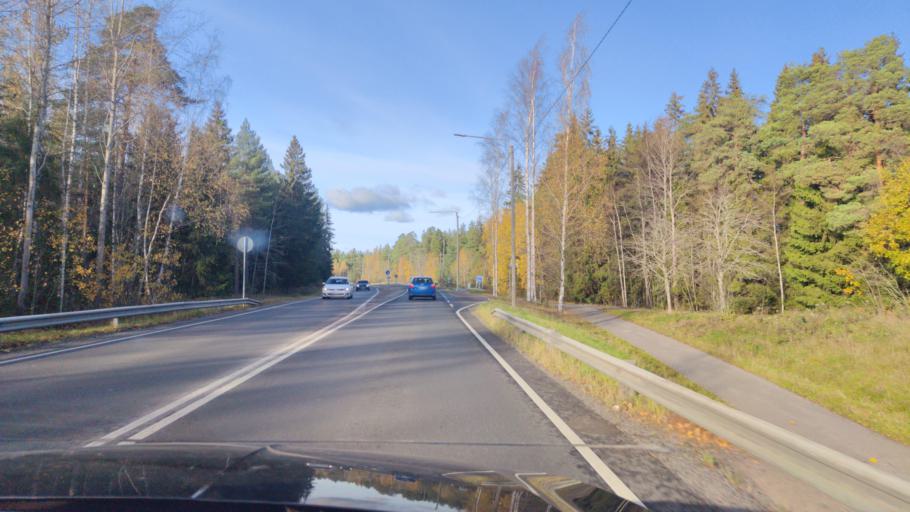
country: FI
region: Varsinais-Suomi
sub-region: Turku
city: Kaarina
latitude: 60.4570
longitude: 22.3663
